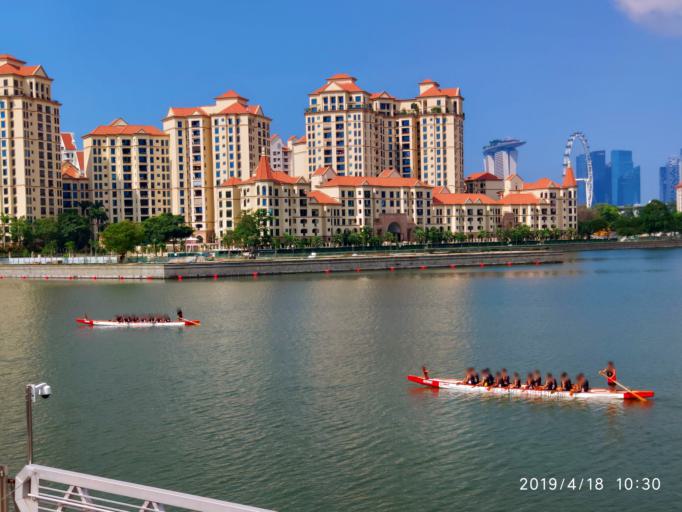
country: SG
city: Singapore
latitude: 1.3009
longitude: 103.8728
